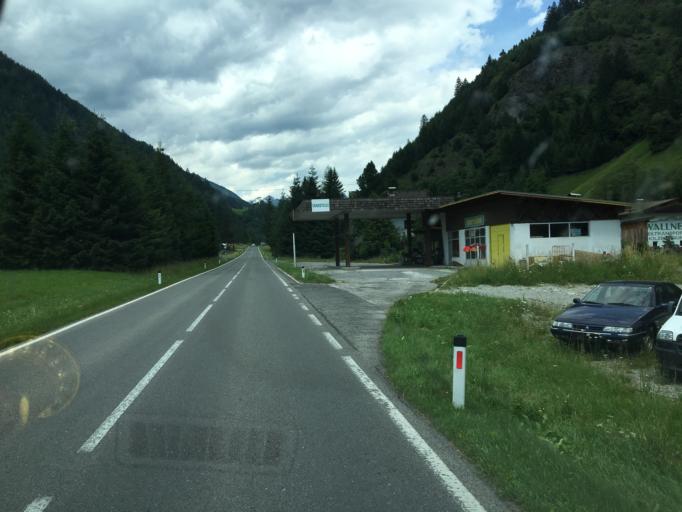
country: AT
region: Carinthia
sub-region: Politischer Bezirk Spittal an der Drau
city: Mortschach
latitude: 46.9362
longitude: 12.9027
